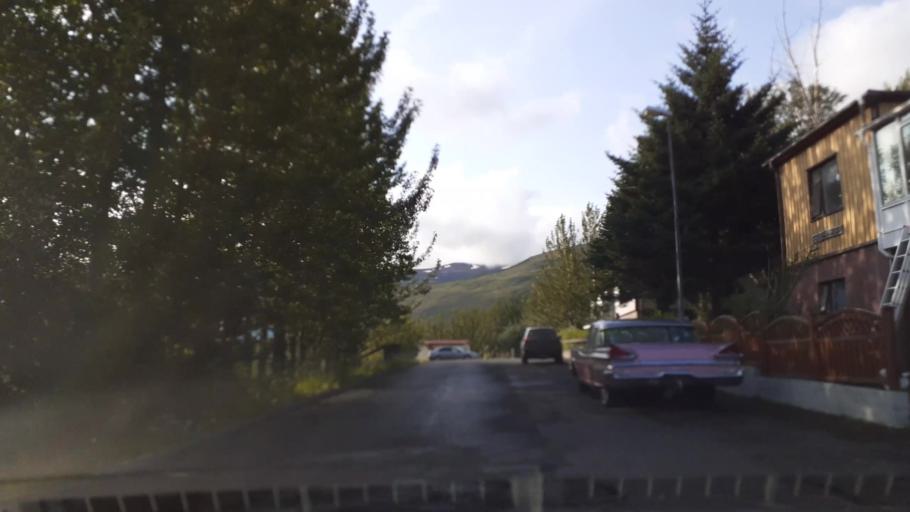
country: IS
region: East
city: Eskifjoerdur
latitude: 65.0672
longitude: -14.0036
